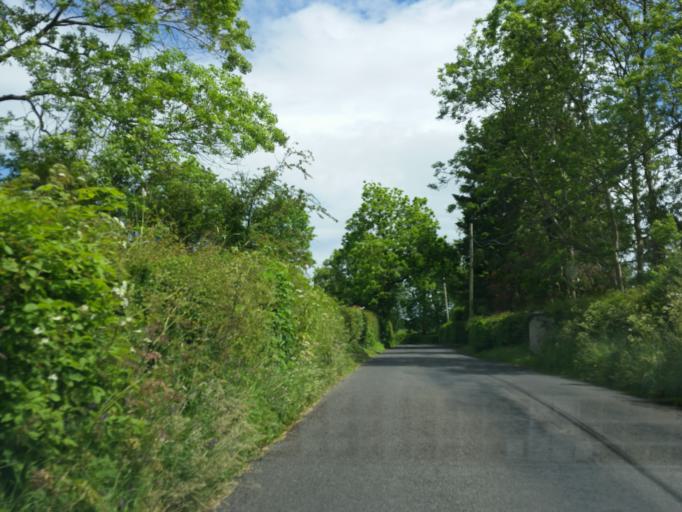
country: GB
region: Northern Ireland
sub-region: Omagh District
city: Omagh
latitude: 54.5515
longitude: -7.1097
